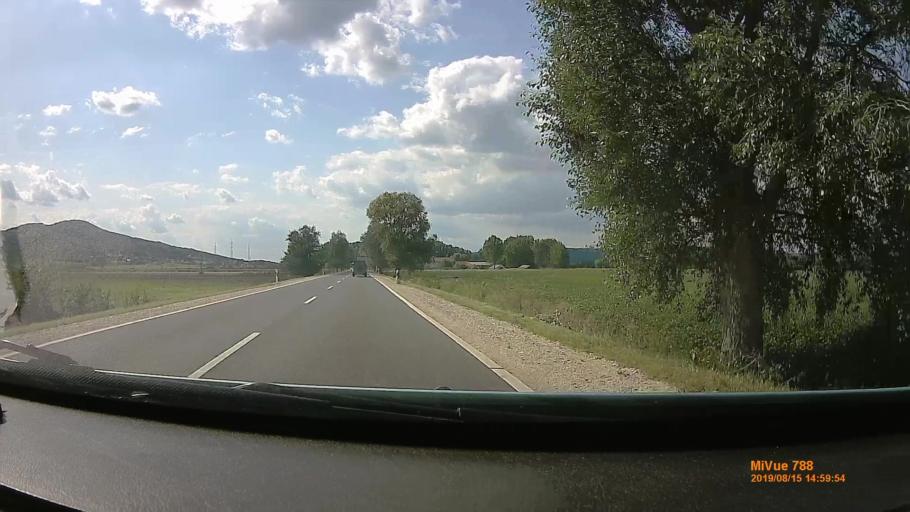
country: HU
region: Borsod-Abauj-Zemplen
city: Sajokaza
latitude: 48.2652
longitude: 20.6069
